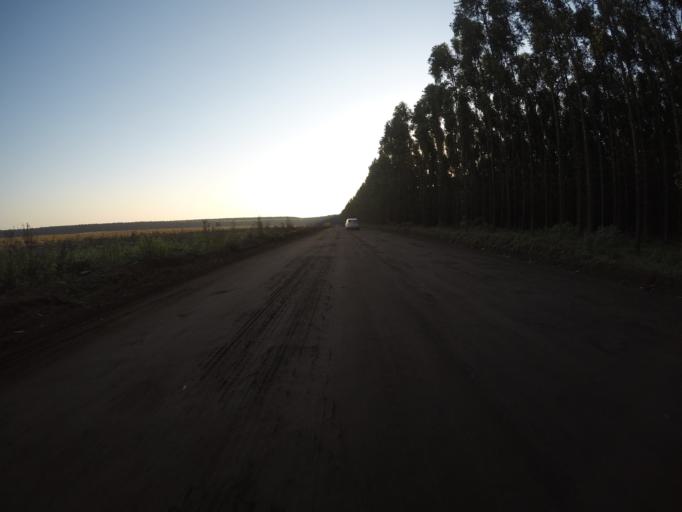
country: ZA
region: KwaZulu-Natal
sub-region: uThungulu District Municipality
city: KwaMbonambi
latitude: -28.6734
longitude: 32.1046
